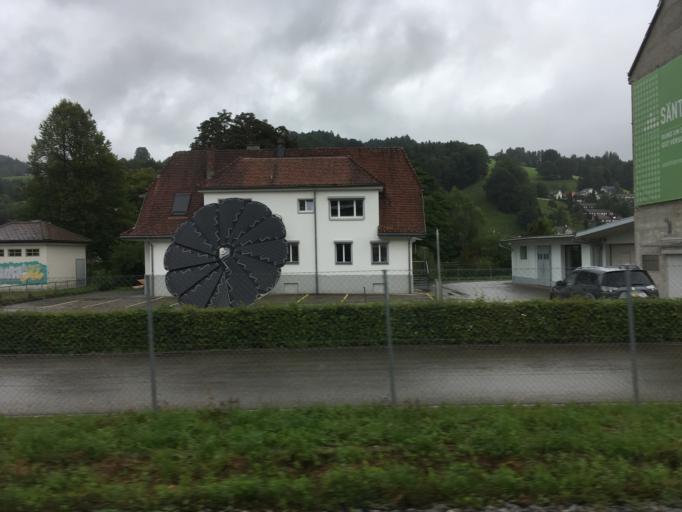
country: CH
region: Saint Gallen
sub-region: Wahlkreis Toggenburg
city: Wattwil
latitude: 47.2955
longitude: 9.0890
